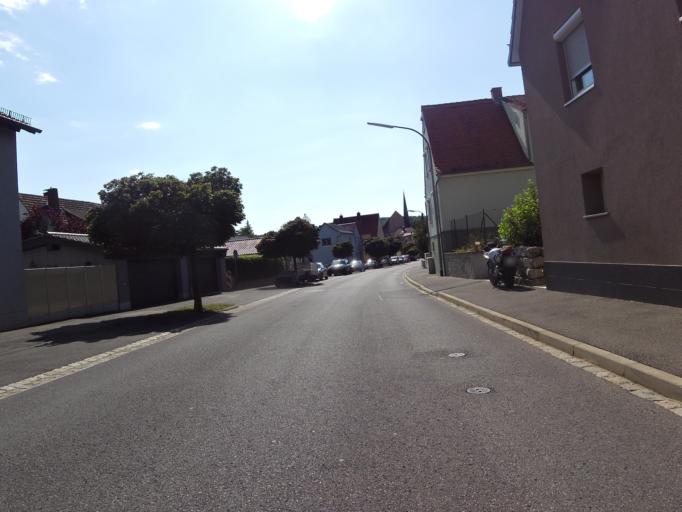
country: DE
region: Bavaria
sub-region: Regierungsbezirk Unterfranken
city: Wuerzburg
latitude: 49.8230
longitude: 9.9679
